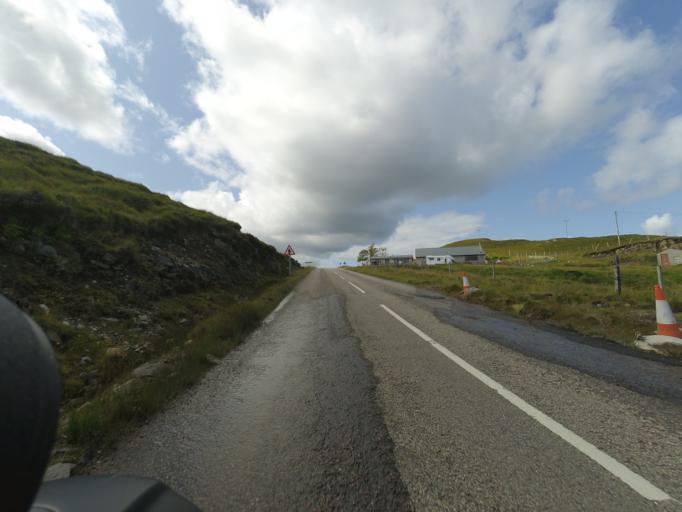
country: GB
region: Scotland
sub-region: Highland
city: Ullapool
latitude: 58.2500
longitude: -5.0103
